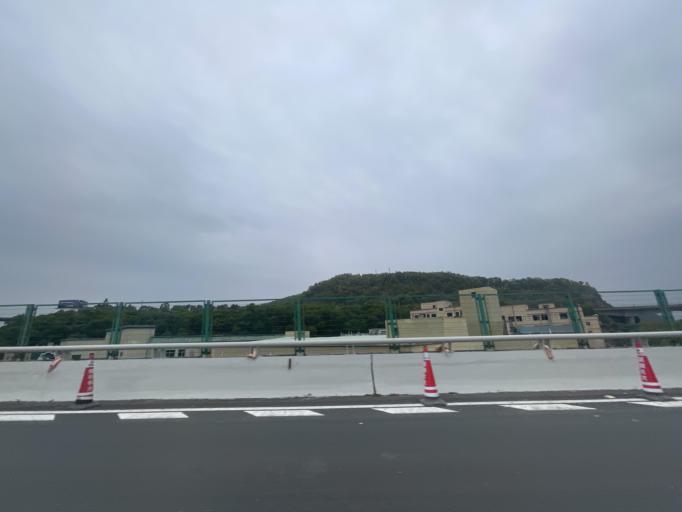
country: CN
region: Guangdong
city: Humen
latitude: 22.8072
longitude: 113.6448
